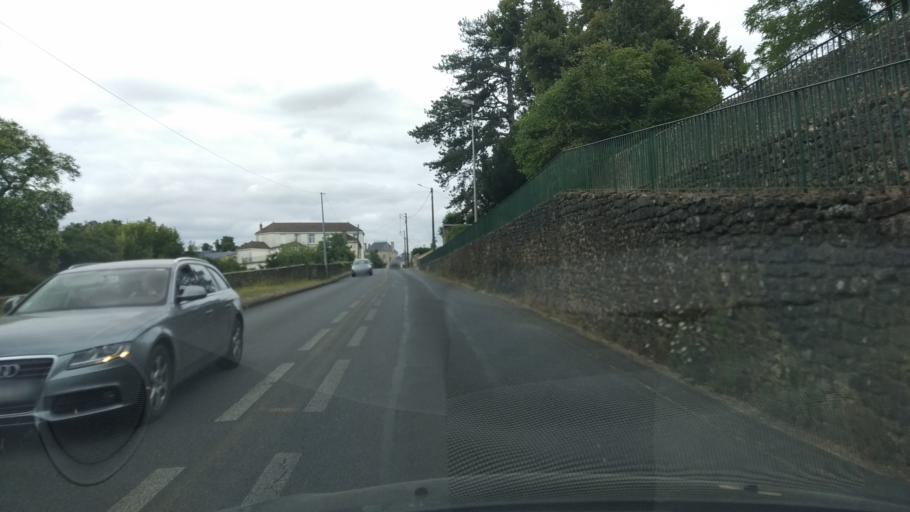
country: FR
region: Poitou-Charentes
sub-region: Departement de la Vienne
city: Roches-Premarie-Andille
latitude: 46.4823
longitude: 0.3707
